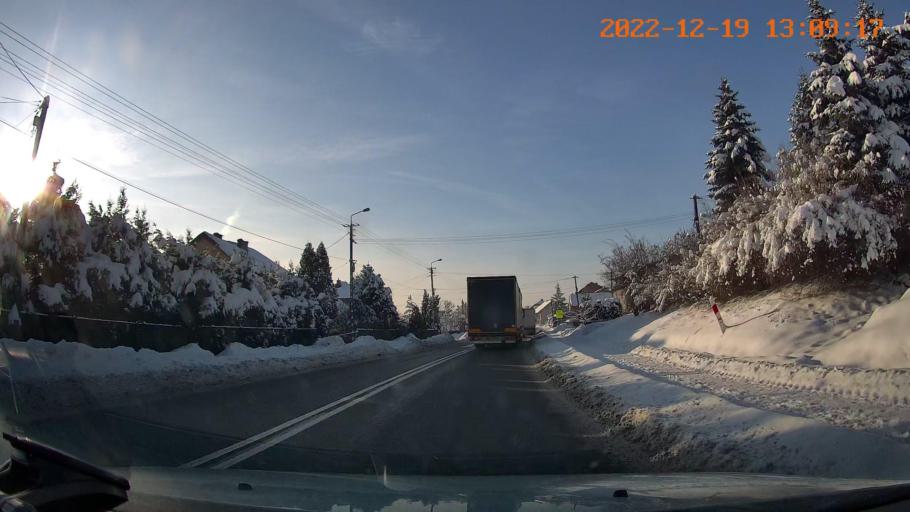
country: PL
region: Lesser Poland Voivodeship
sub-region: Powiat oswiecimski
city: Chelmek
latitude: 50.0979
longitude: 19.2414
